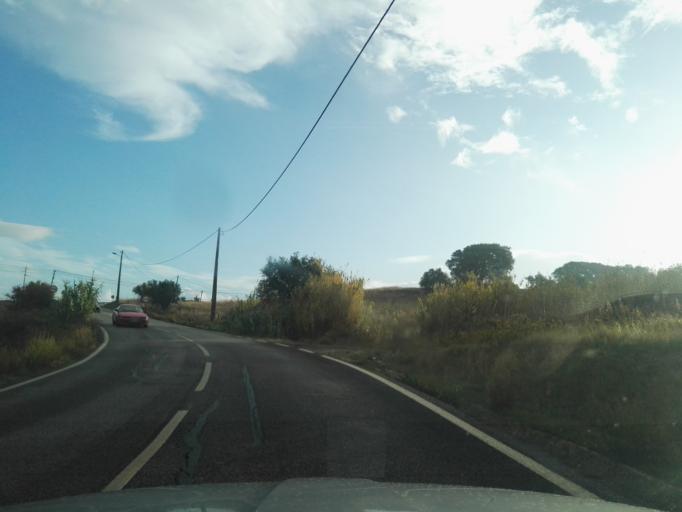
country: PT
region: Lisbon
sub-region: Arruda Dos Vinhos
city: Arruda dos Vinhos
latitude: 38.9745
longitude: -9.0531
